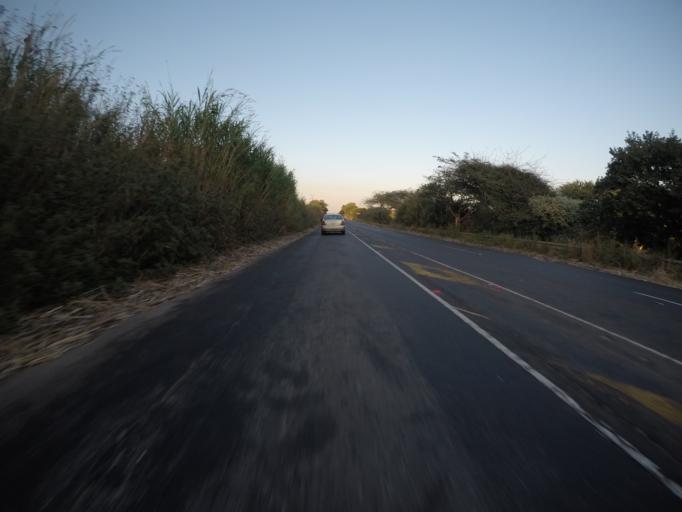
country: ZA
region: KwaZulu-Natal
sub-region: uThungulu District Municipality
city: Empangeni
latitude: -28.8151
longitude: 31.8885
